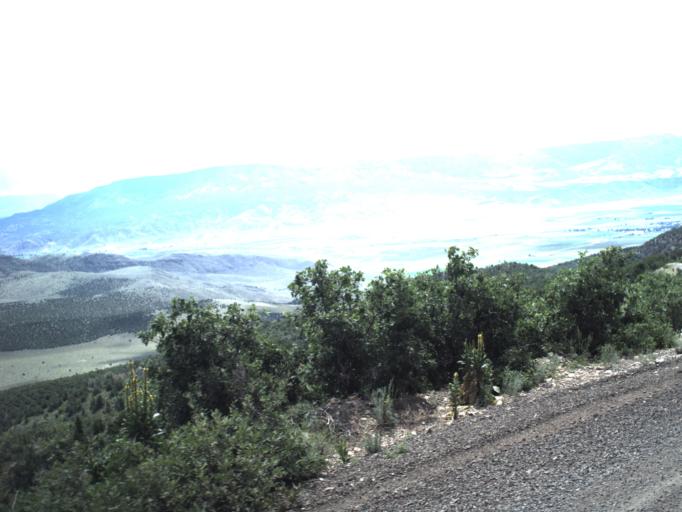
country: US
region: Utah
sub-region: Piute County
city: Junction
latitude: 38.2563
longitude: -112.3157
